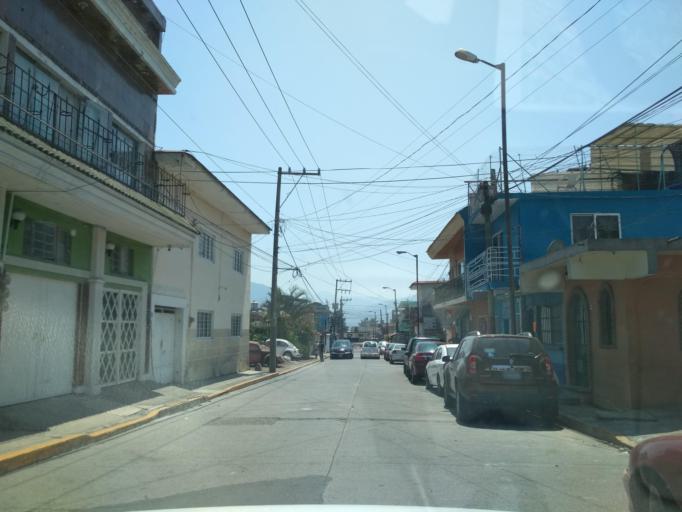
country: MX
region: Veracruz
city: Orizaba
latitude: 18.8491
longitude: -97.0865
